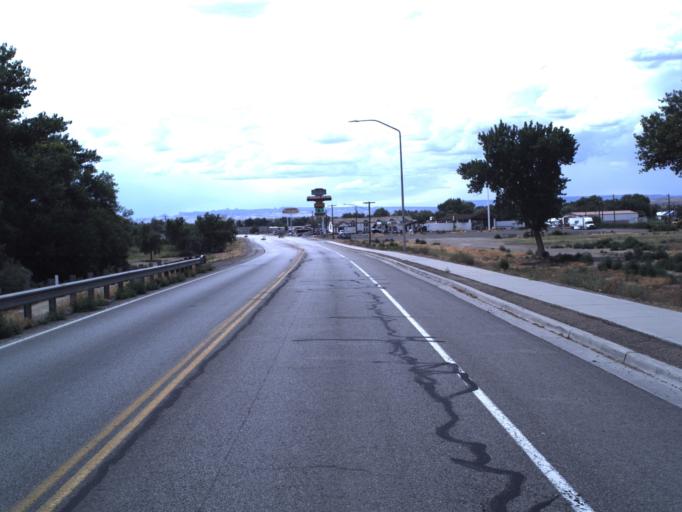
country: US
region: Utah
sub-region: Carbon County
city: East Carbon City
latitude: 38.9940
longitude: -110.1444
